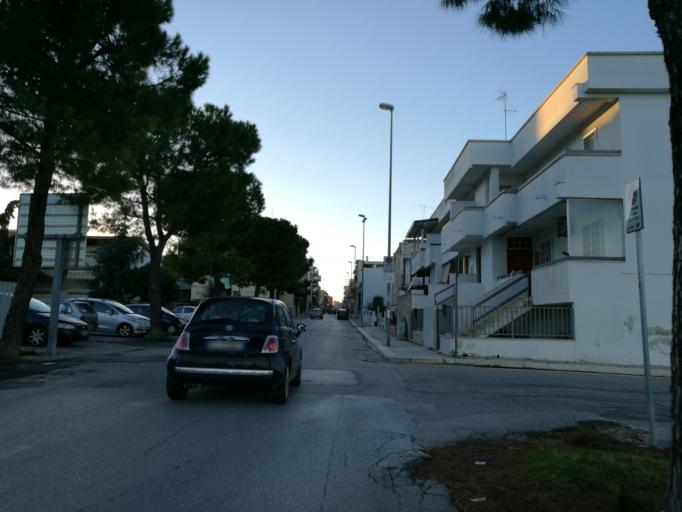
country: IT
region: Apulia
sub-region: Provincia di Bari
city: Adelfia
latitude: 41.0040
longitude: 16.8822
